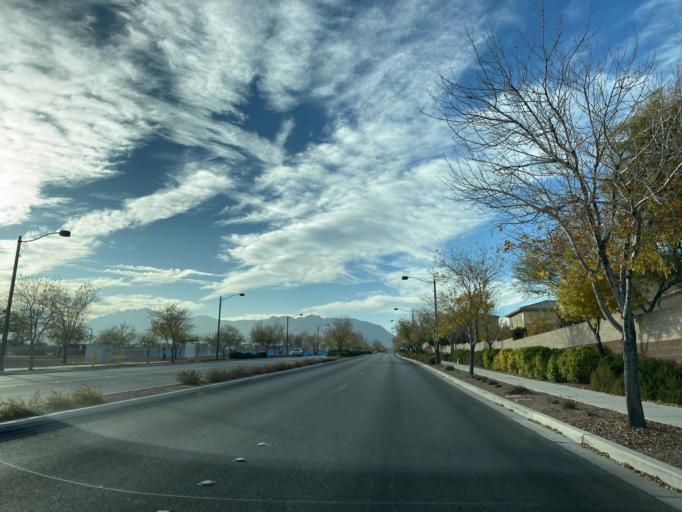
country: US
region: Nevada
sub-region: Clark County
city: Summerlin South
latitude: 36.2994
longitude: -115.3200
